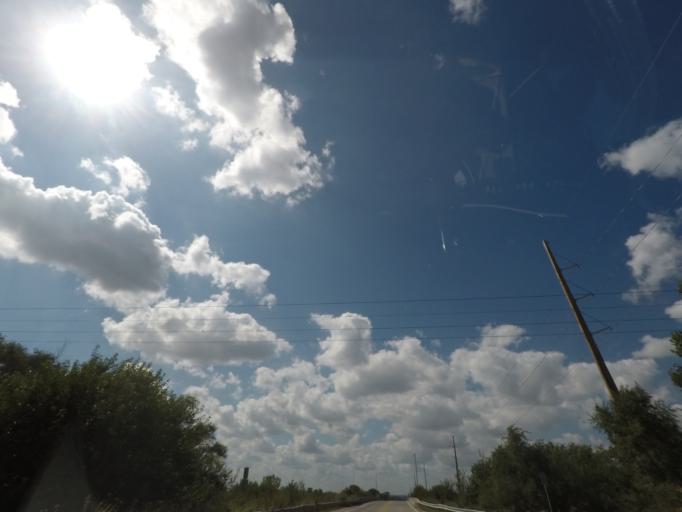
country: US
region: Iowa
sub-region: Story County
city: Ames
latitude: 42.0228
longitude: -93.5701
